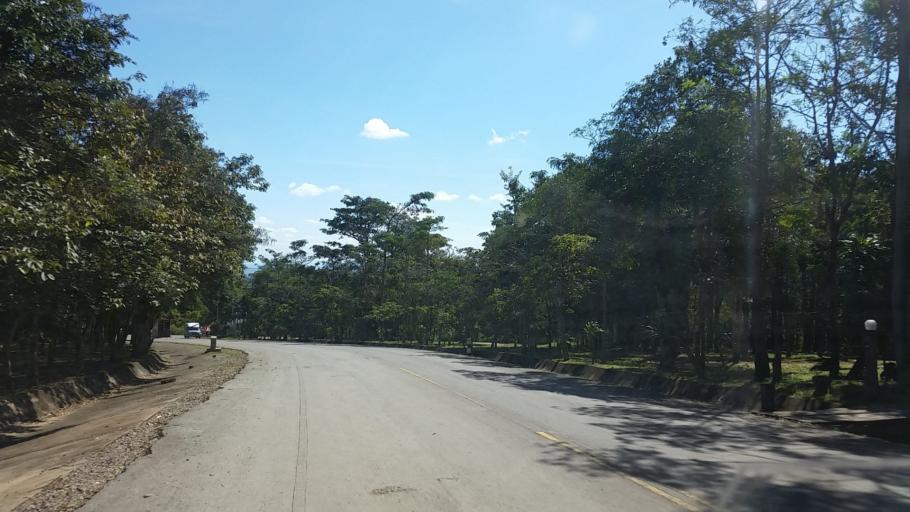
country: TH
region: Chaiyaphum
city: Sap Yai
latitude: 15.6308
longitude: 101.3944
